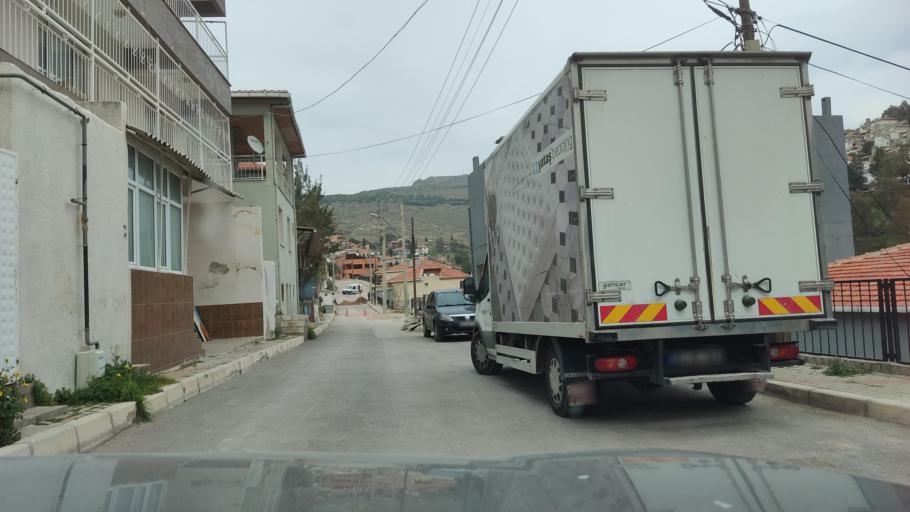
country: TR
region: Izmir
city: Karsiyaka
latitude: 38.4984
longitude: 27.0774
